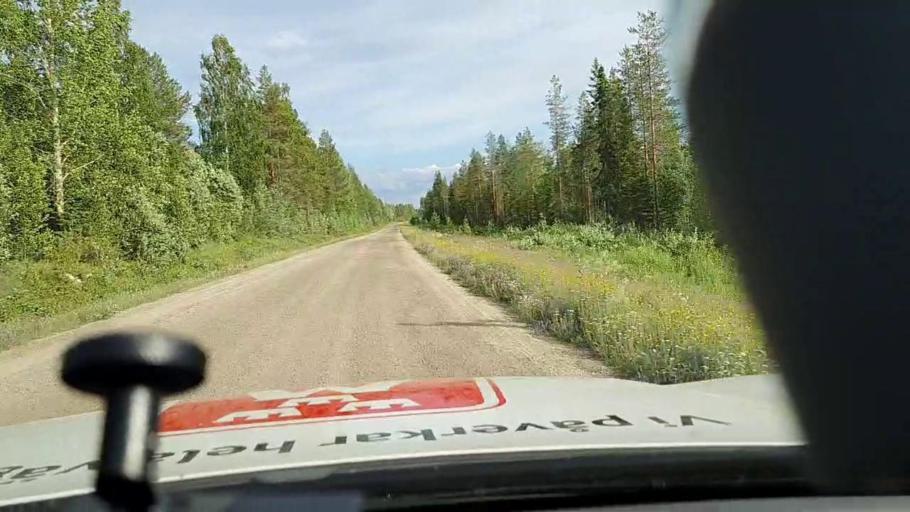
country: SE
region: Norrbotten
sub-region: Alvsbyns Kommun
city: AElvsbyn
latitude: 66.1801
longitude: 21.2293
